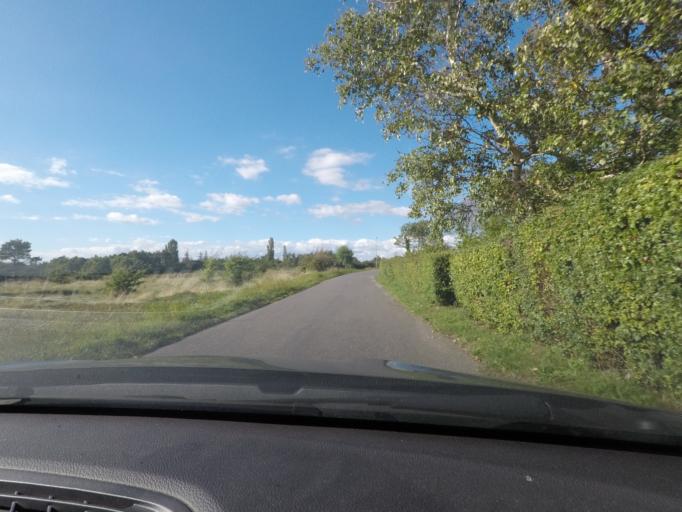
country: DK
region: Zealand
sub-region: Lolland Kommune
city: Maribo
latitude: 54.9749
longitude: 11.5130
